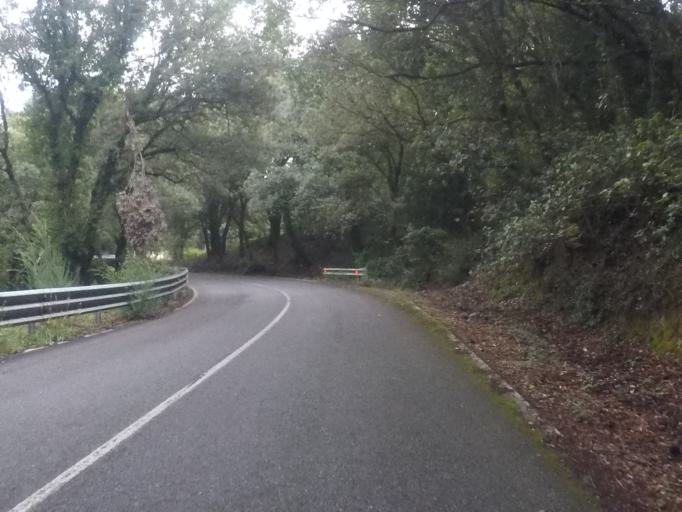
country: IT
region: Sardinia
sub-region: Provincia di Oristano
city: Cuglieri
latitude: 40.1706
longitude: 8.6067
